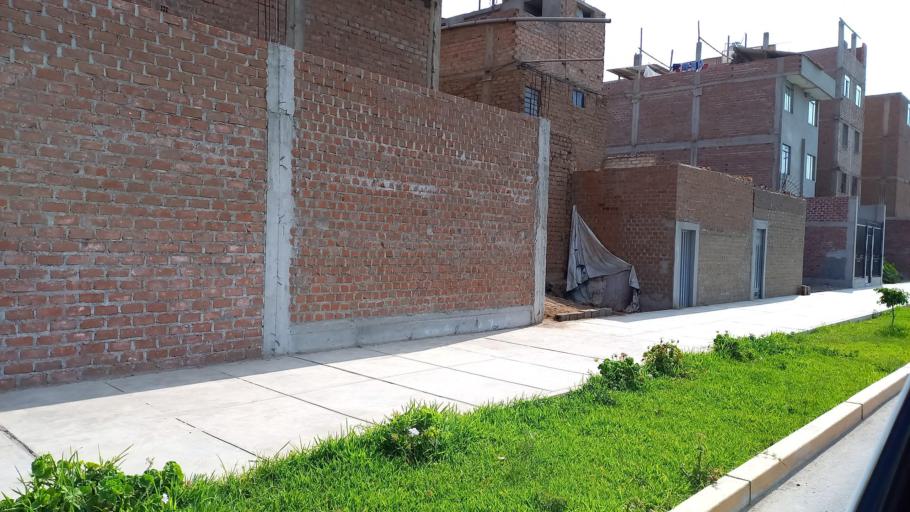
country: PE
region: La Libertad
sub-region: Provincia de Trujillo
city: La Esperanza
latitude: -8.1013
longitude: -79.0547
